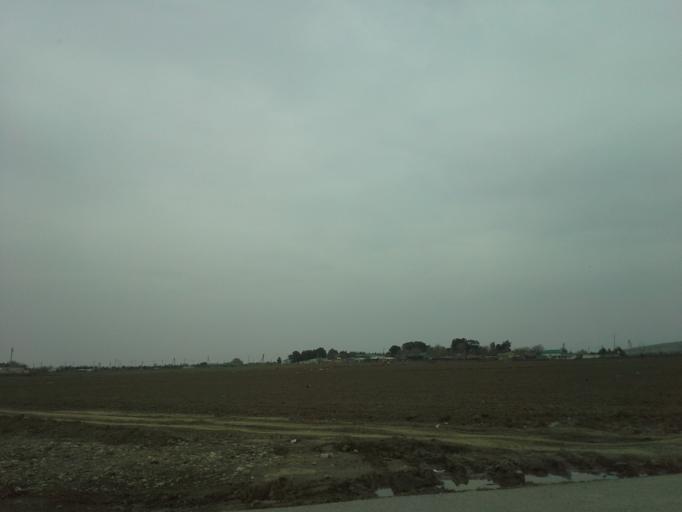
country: TM
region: Ahal
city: Abadan
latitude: 37.9741
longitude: 58.2290
